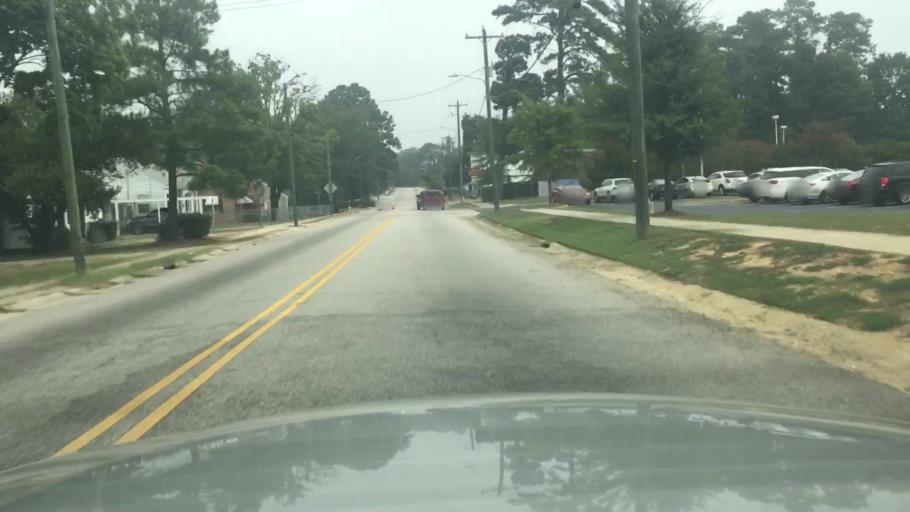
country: US
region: North Carolina
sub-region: Cumberland County
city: Fayetteville
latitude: 35.0732
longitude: -78.8833
